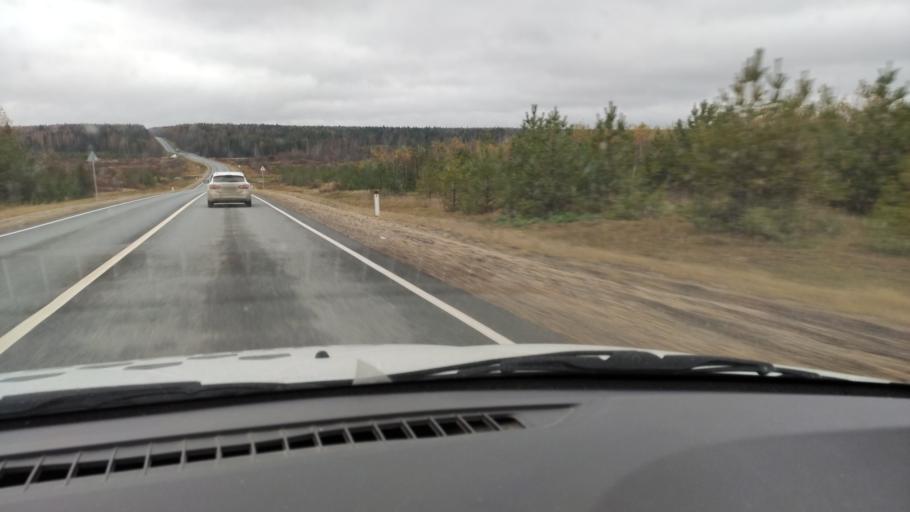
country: RU
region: Kirov
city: Chernaya Kholunitsa
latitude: 58.8587
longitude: 51.7023
